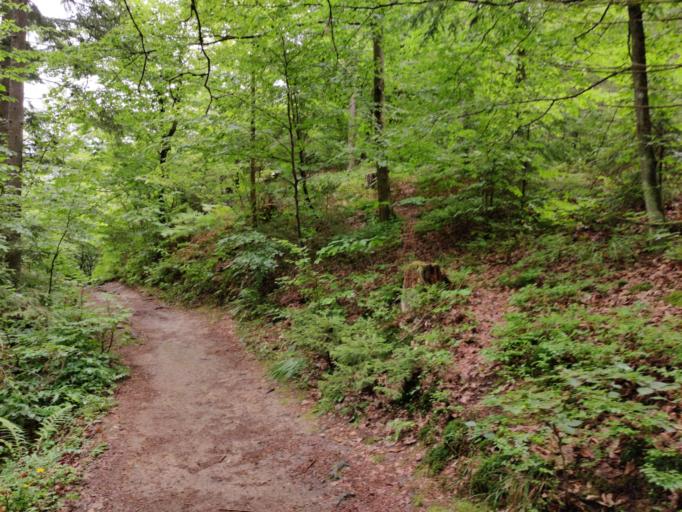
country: AT
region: Carinthia
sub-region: Klagenfurt am Woerthersee
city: Klagenfurt am Woerthersee
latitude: 46.6317
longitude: 14.2689
